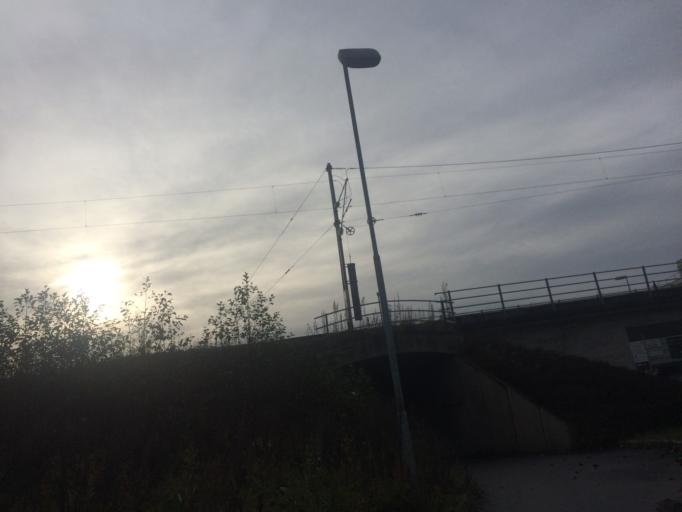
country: NO
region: Akershus
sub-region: Ski
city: Ski
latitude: 59.7150
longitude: 10.8384
